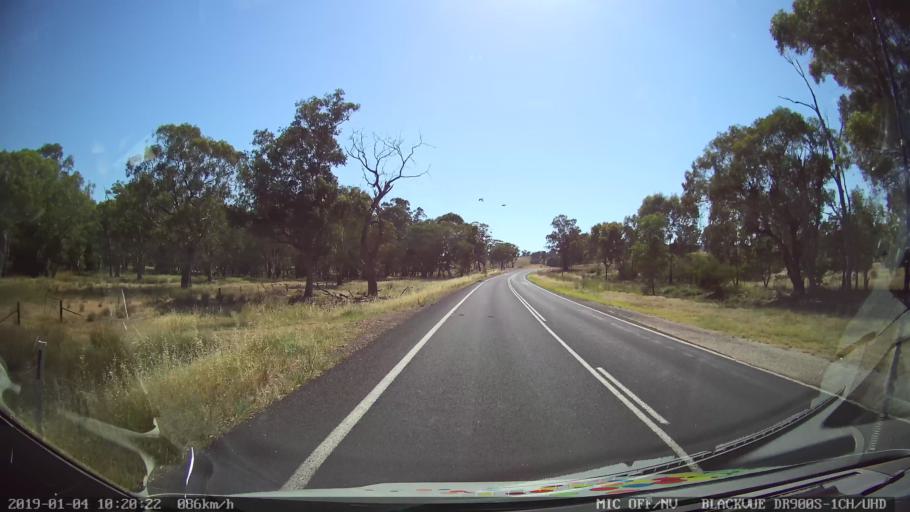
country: AU
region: New South Wales
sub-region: Cabonne
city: Canowindra
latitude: -33.3722
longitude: 148.4947
